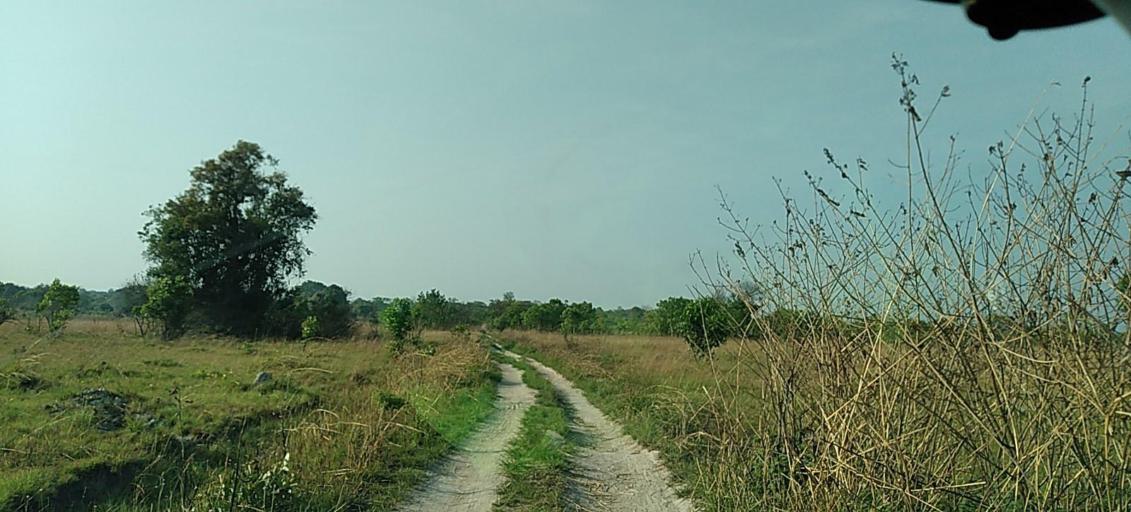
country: ZM
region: North-Western
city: Kalengwa
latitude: -13.1639
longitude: 25.0351
